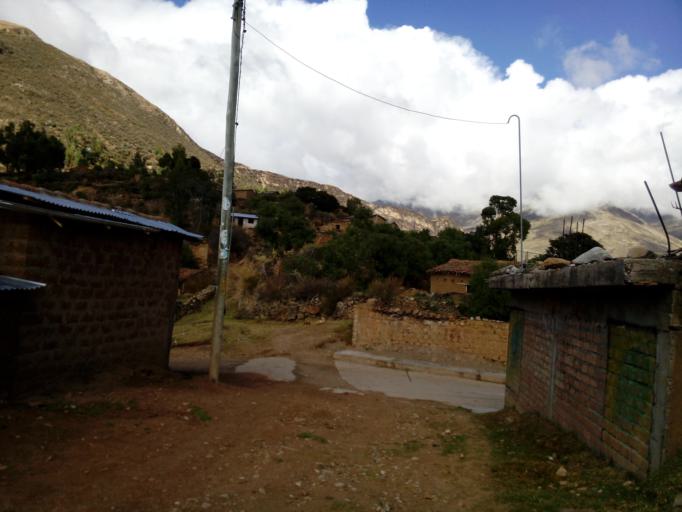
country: PE
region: Ayacucho
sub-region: Provincia de Victor Fajardo
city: Canaria
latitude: -13.8798
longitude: -73.9302
